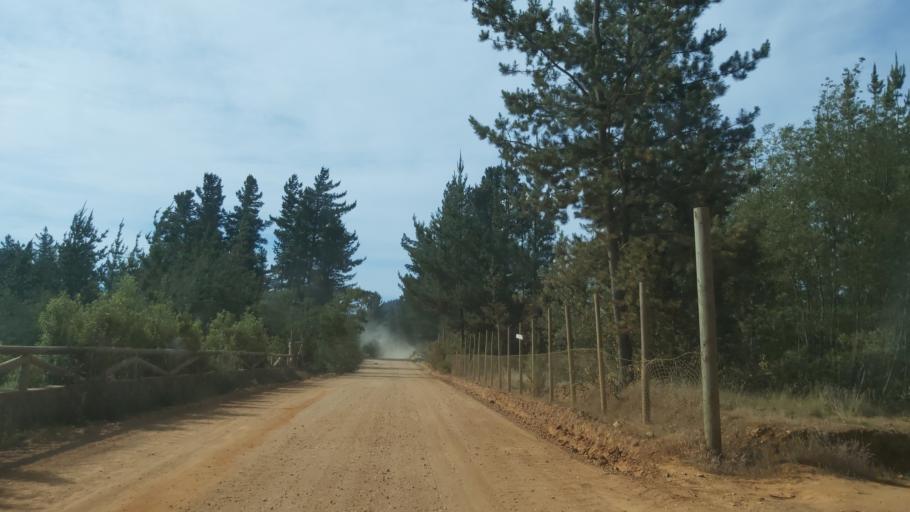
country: CL
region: Maule
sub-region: Provincia de Talca
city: Constitucion
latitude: -34.8441
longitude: -72.0384
